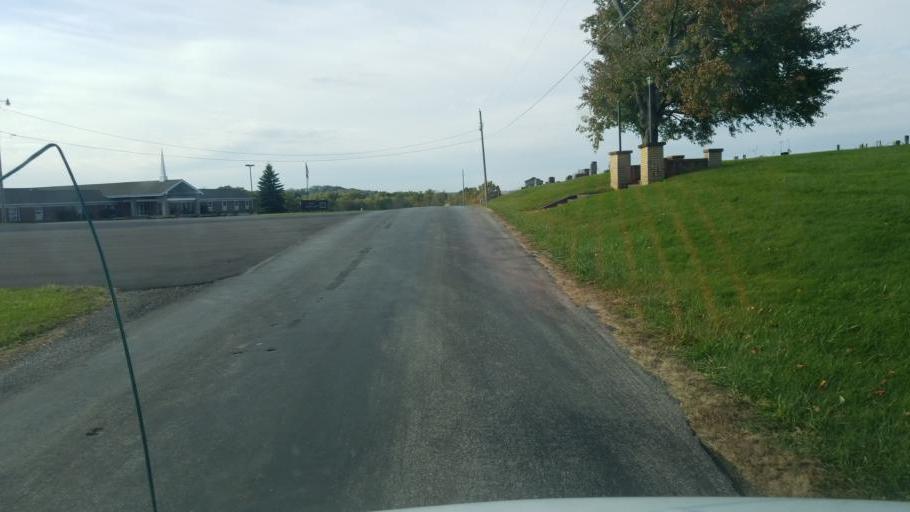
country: US
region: Ohio
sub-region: Wayne County
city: Shreve
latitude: 40.6511
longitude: -82.0621
